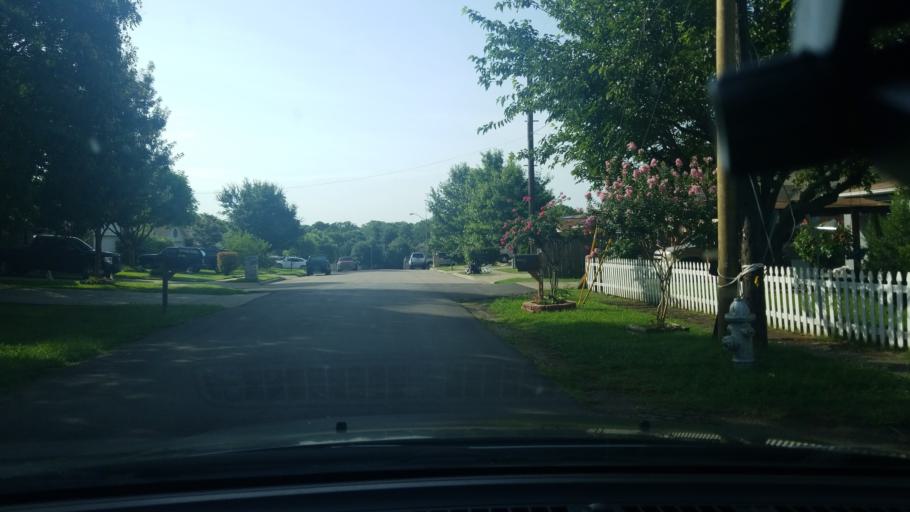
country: US
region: Texas
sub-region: Dallas County
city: Highland Park
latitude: 32.7988
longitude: -96.7151
